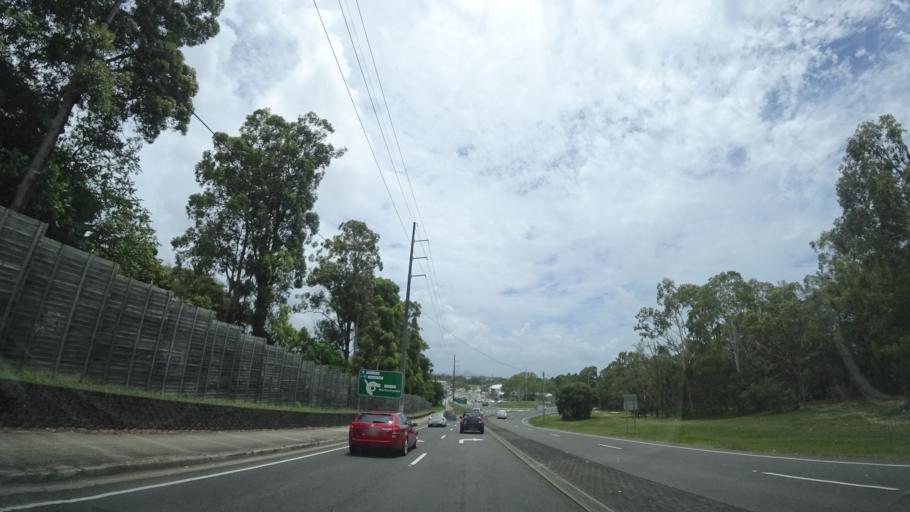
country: AU
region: Queensland
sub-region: Sunshine Coast
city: Mooloolaba
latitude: -26.6750
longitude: 153.0956
